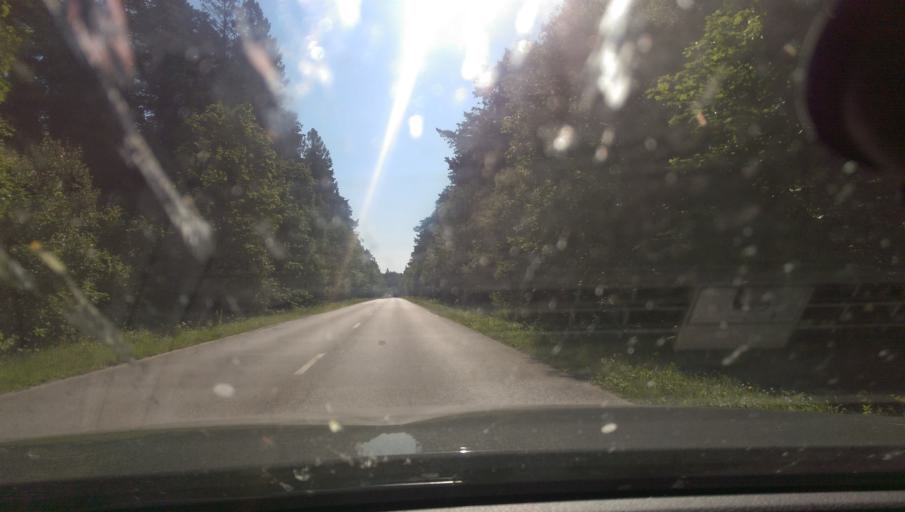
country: LT
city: Priekule
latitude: 55.6368
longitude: 21.3244
